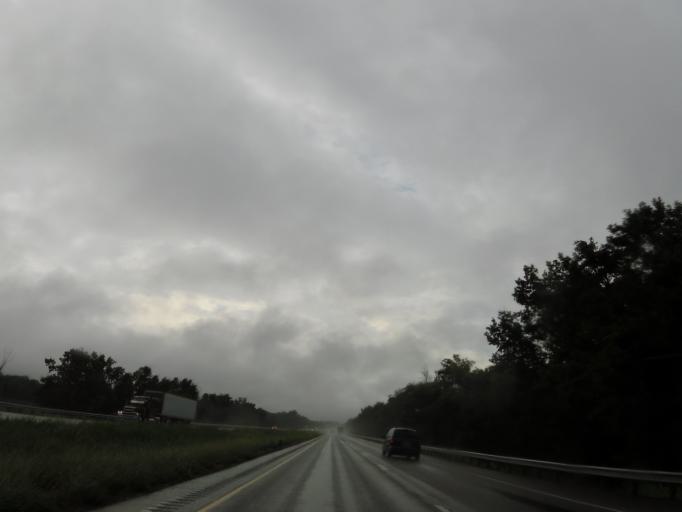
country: US
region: Illinois
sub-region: Franklin County
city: West Frankfort
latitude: 37.9200
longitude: -88.9465
